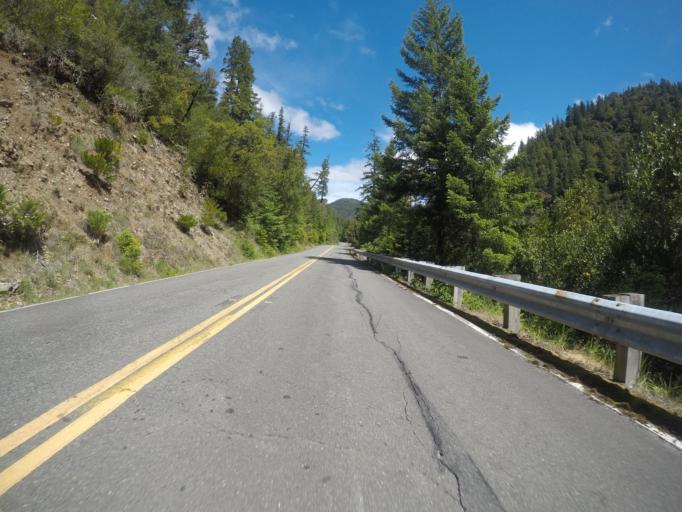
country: US
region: California
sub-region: Del Norte County
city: Bertsch-Oceanview
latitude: 41.7086
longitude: -123.9414
